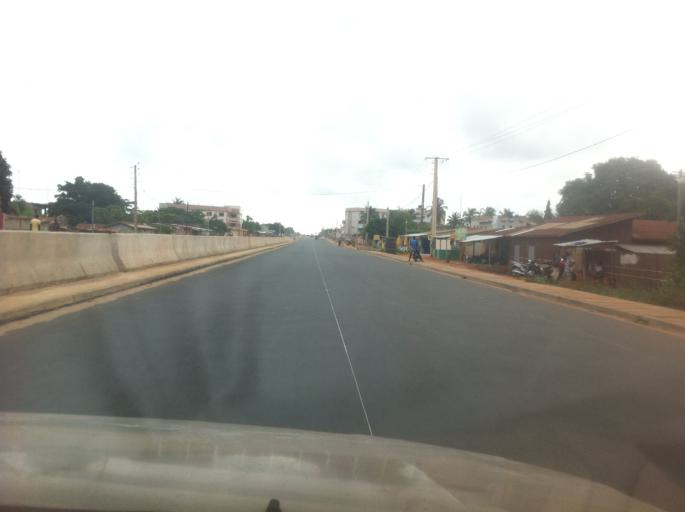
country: BJ
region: Atlantique
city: Ouidah
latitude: 6.3707
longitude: 2.0710
